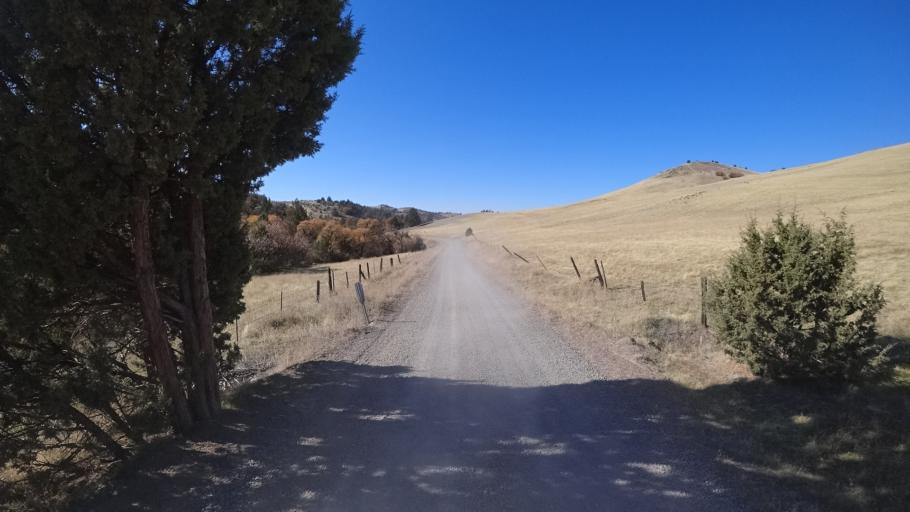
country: US
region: California
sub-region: Siskiyou County
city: Montague
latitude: 41.7935
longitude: -122.3467
